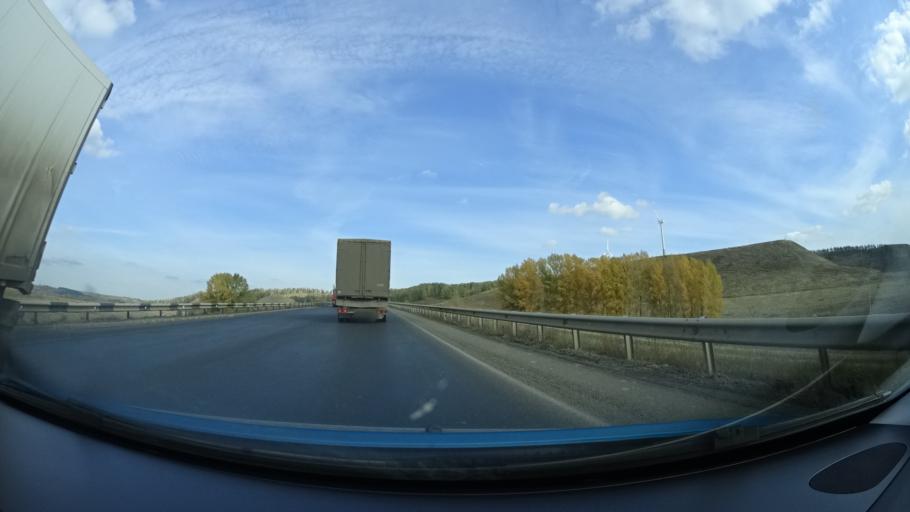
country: RU
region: Bashkortostan
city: Kandry
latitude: 54.5787
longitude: 54.2364
